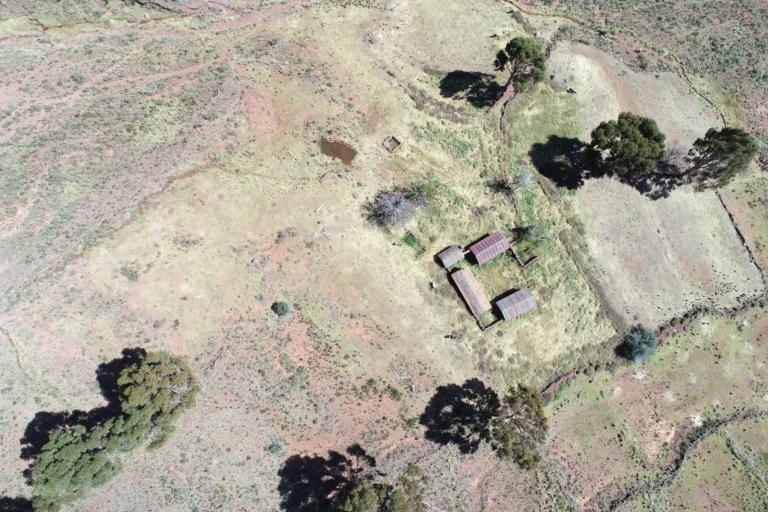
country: BO
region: La Paz
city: Tiahuanaco
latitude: -16.6046
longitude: -68.7720
